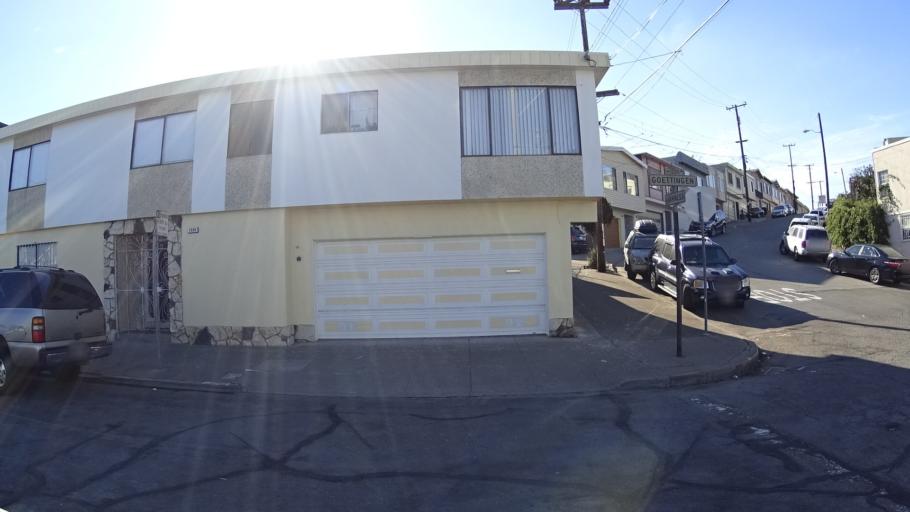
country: US
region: California
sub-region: San Mateo County
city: Brisbane
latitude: 37.7172
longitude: -122.4025
